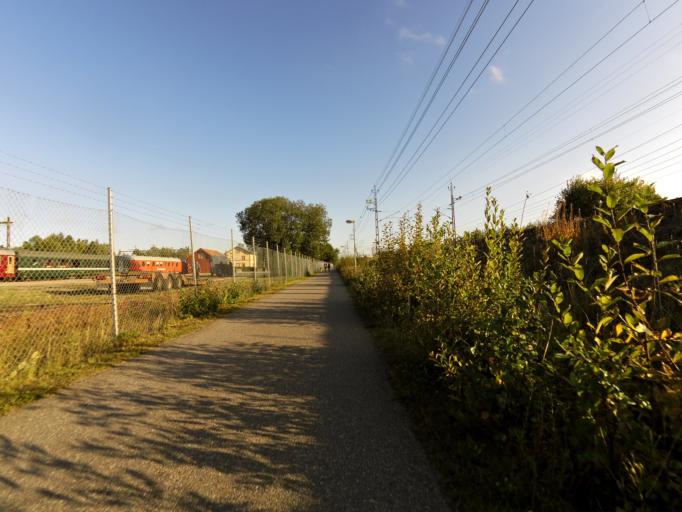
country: SE
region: Gaevleborg
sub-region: Gavle Kommun
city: Gavle
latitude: 60.6640
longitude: 17.1676
